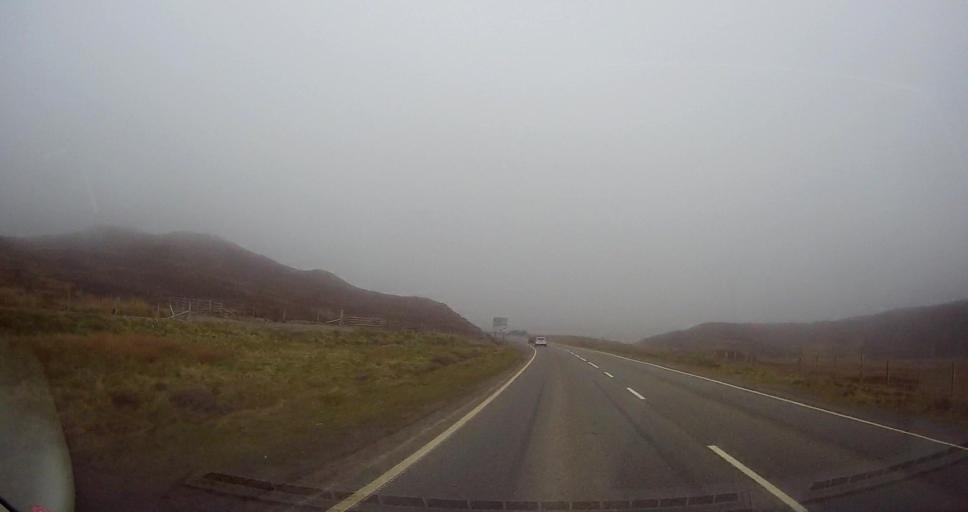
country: GB
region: Scotland
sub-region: Shetland Islands
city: Lerwick
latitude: 60.1416
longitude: -1.2525
